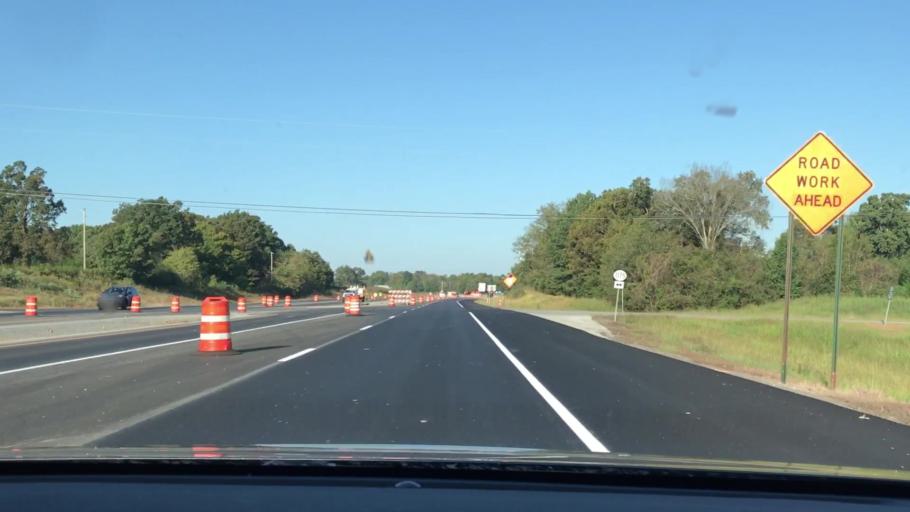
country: US
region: Kentucky
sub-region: Trigg County
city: Cadiz
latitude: 36.8386
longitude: -87.8506
